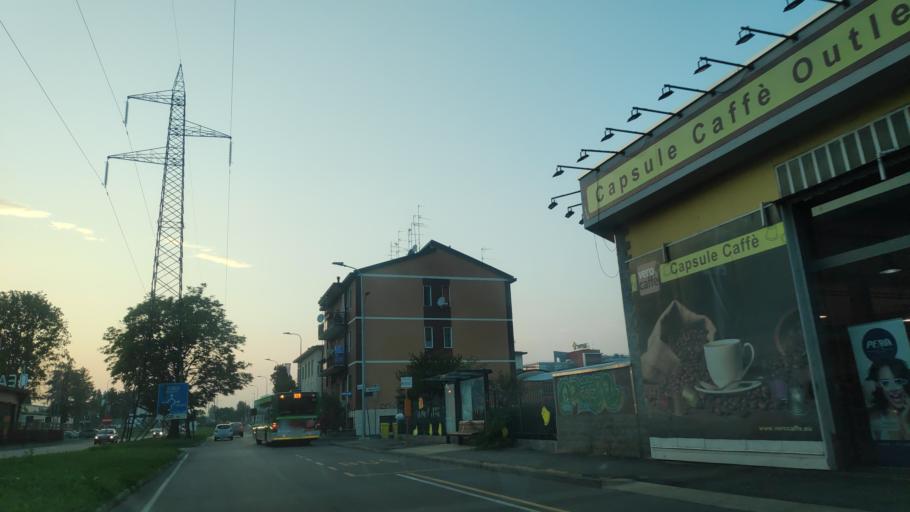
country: IT
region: Lombardy
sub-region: Citta metropolitana di Milano
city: Rozzano
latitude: 45.3946
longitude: 9.1549
